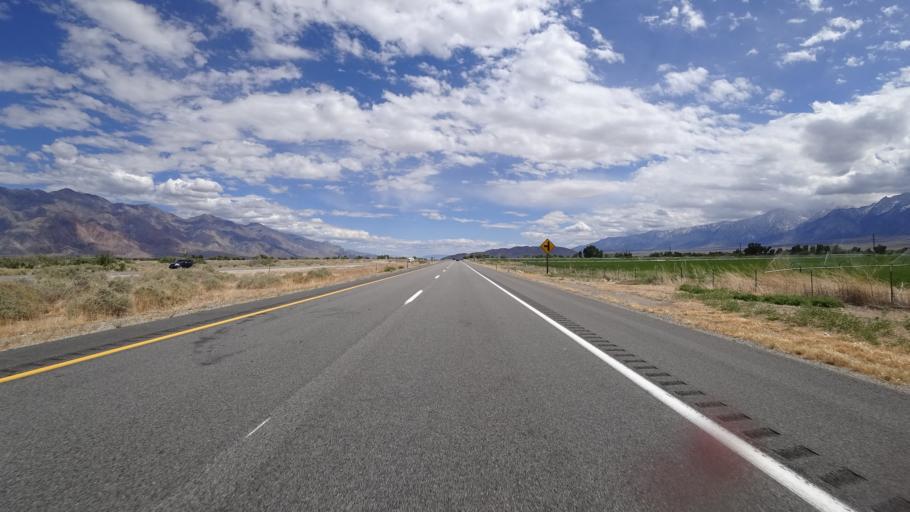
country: US
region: California
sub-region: Inyo County
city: Lone Pine
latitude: 36.7479
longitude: -118.1564
